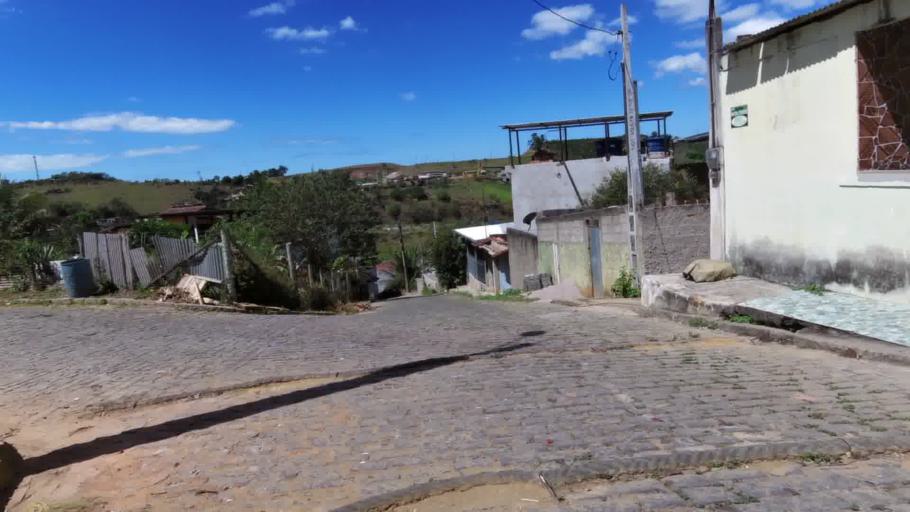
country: BR
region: Espirito Santo
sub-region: Rio Novo Do Sul
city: Rio Novo do Sul
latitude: -20.8666
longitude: -40.9422
